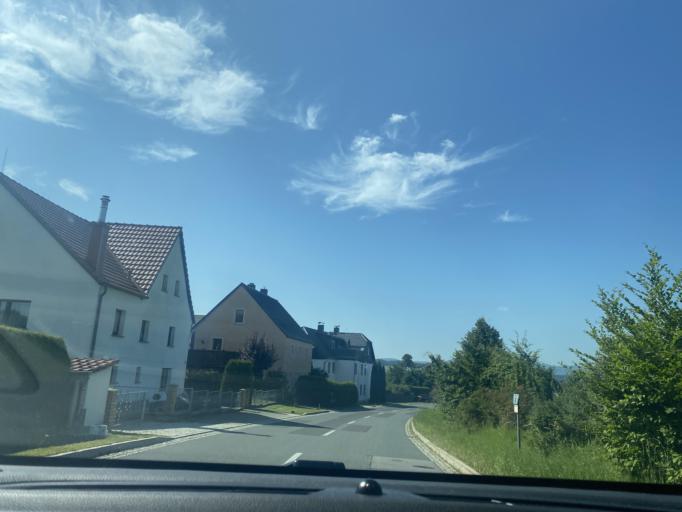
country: DE
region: Saxony
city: Mittelherwigsdorf
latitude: 50.9592
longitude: 14.7342
